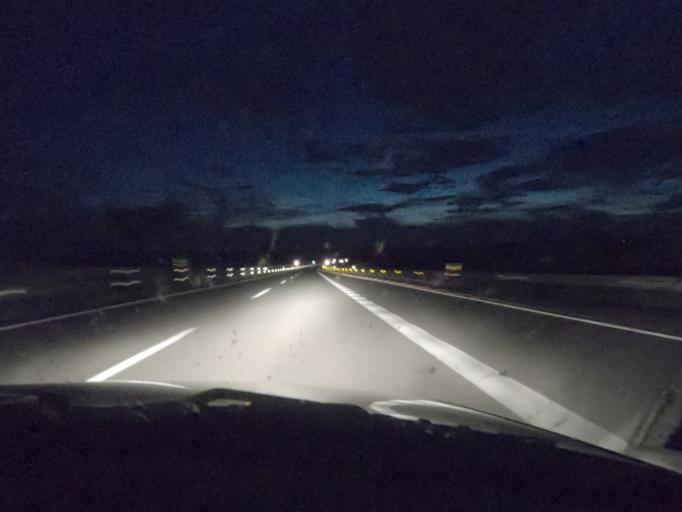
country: ES
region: Extremadura
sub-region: Provincia de Caceres
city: Casas de Don Gomez
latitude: 40.0113
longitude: -6.5667
